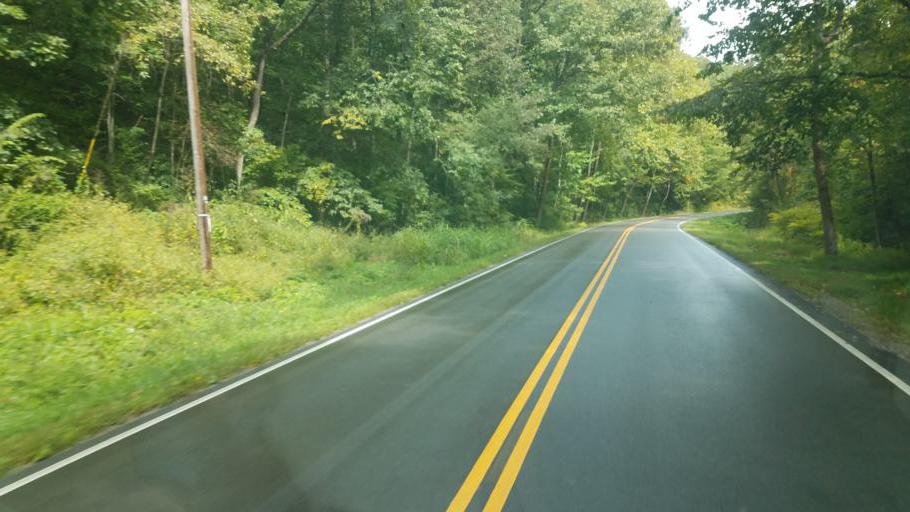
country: US
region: Ohio
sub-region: Scioto County
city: Sciotodale
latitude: 38.8808
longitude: -82.7943
